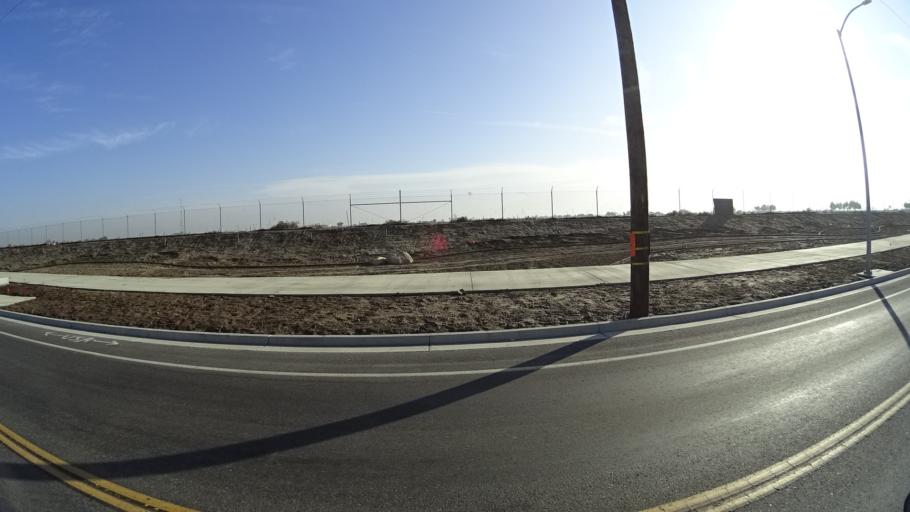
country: US
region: California
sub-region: Kern County
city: Greenfield
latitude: 35.2745
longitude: -119.0921
